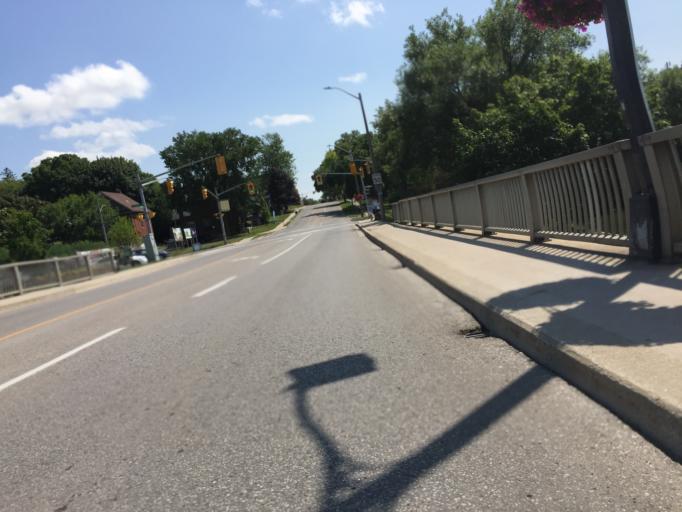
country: CA
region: Ontario
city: Stratford
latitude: 43.3738
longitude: -80.9797
